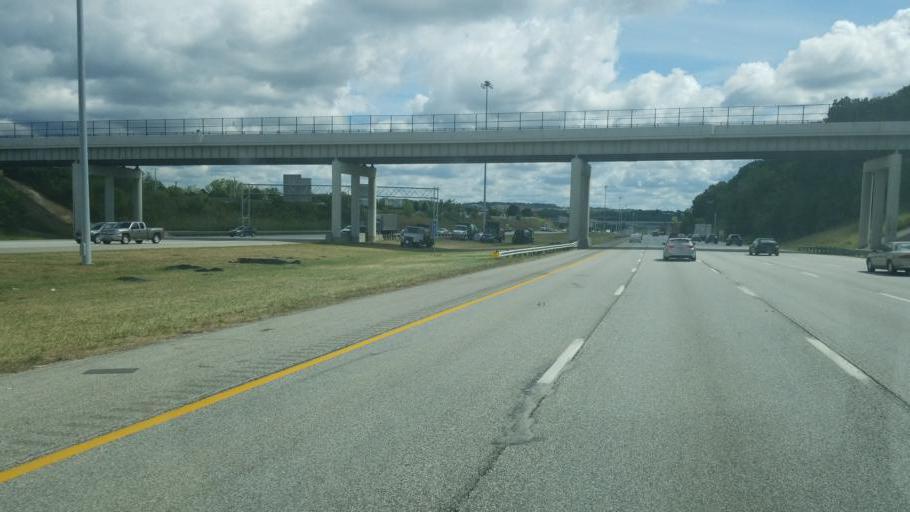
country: US
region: Ohio
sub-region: Cuyahoga County
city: Seven Hills
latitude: 41.4107
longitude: -81.6674
